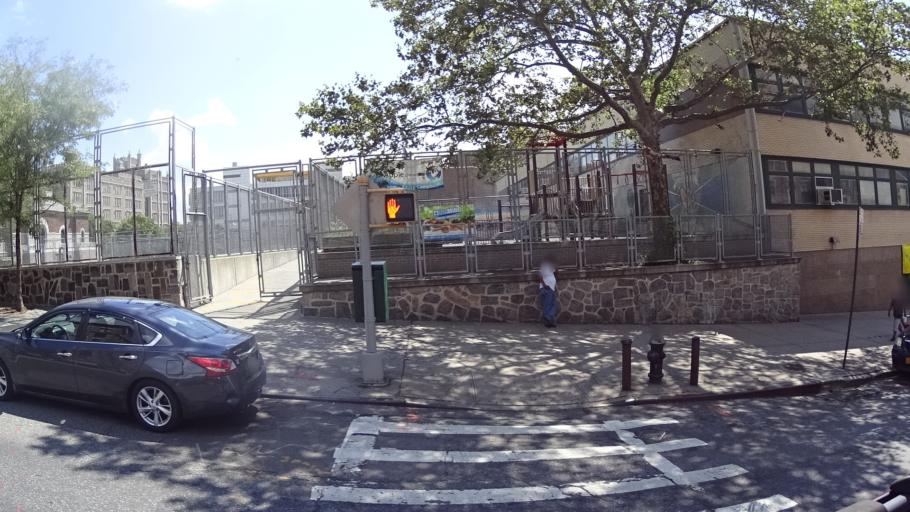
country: US
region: New Jersey
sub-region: Bergen County
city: Edgewater
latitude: 40.8181
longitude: -73.9528
